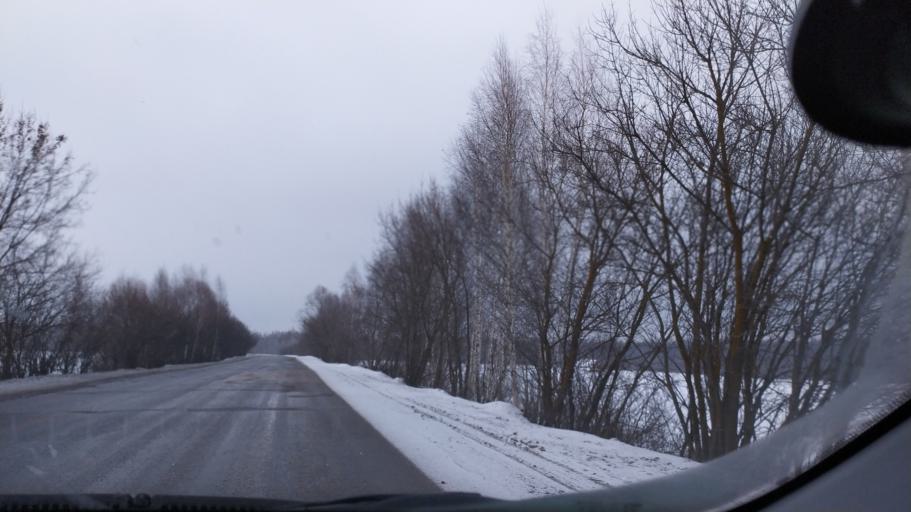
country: RU
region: Mariy-El
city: Krasnogorskiy
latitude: 56.1521
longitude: 48.1520
